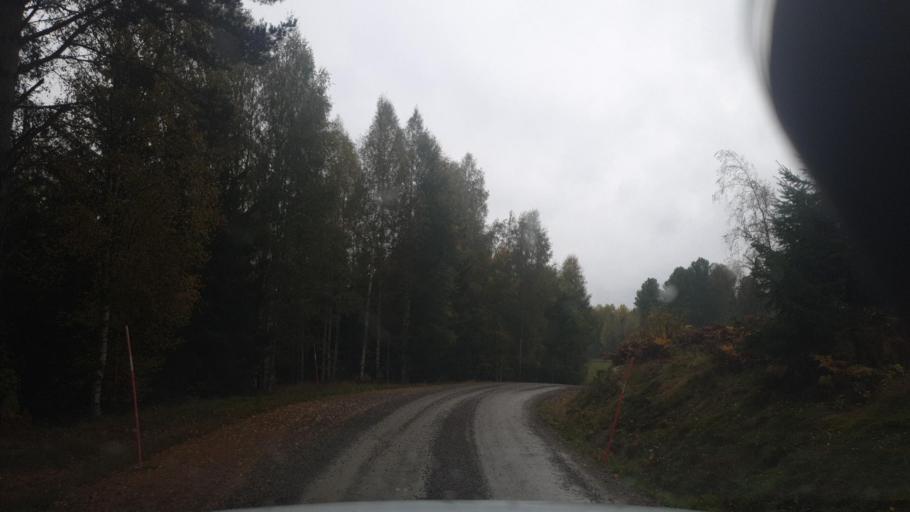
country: SE
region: Vaermland
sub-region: Eda Kommun
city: Amotfors
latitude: 59.8402
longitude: 12.5345
